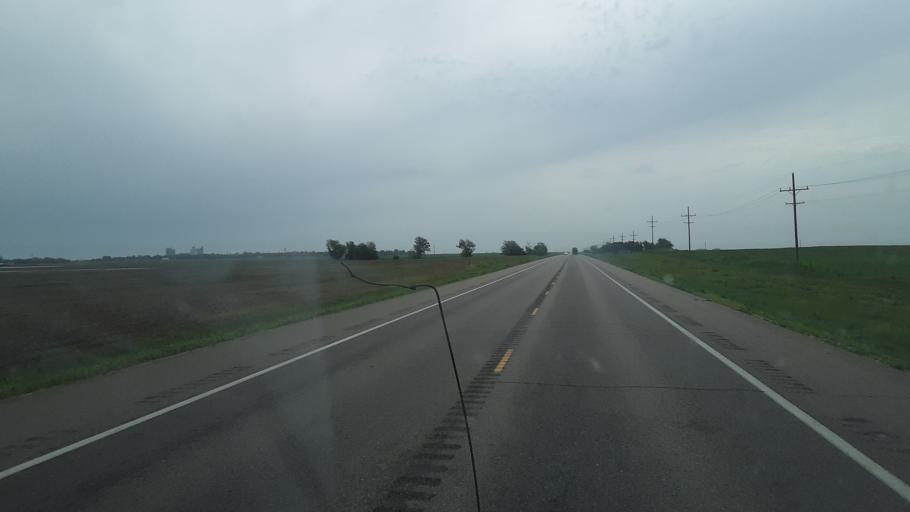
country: US
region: Kansas
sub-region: Edwards County
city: Kinsley
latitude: 37.9275
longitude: -99.2838
